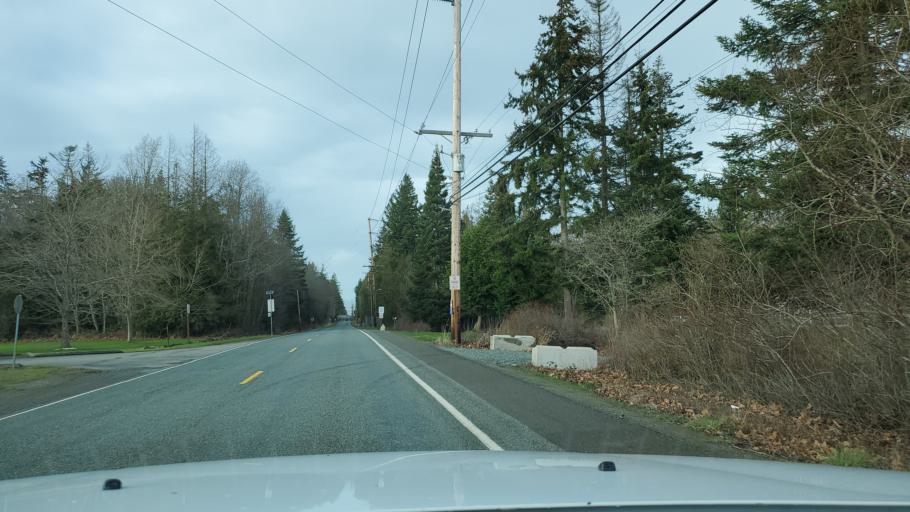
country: US
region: Washington
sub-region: Skagit County
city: Anacortes
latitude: 48.4471
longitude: -122.5817
